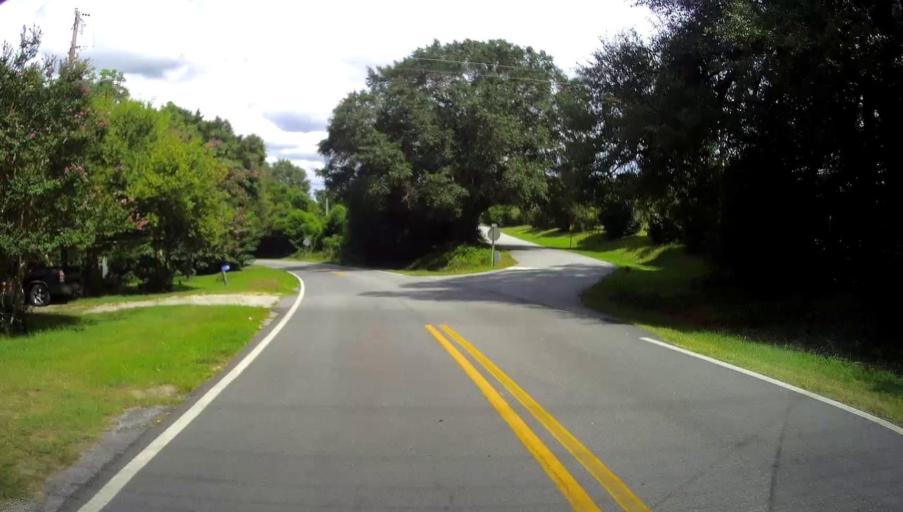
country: US
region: Georgia
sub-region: Chattahoochee County
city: Cusseta
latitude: 32.3048
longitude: -84.7720
